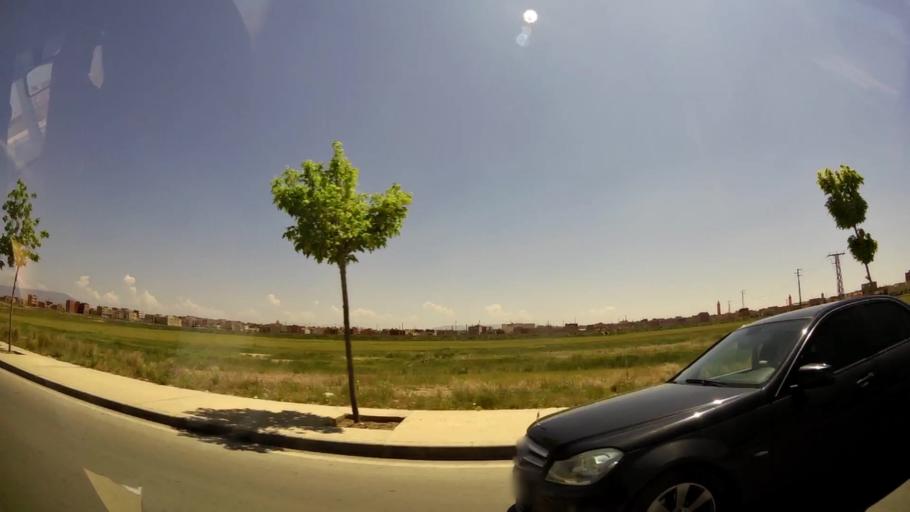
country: MA
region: Oriental
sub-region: Oujda-Angad
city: Oujda
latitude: 34.6958
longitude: -1.9344
